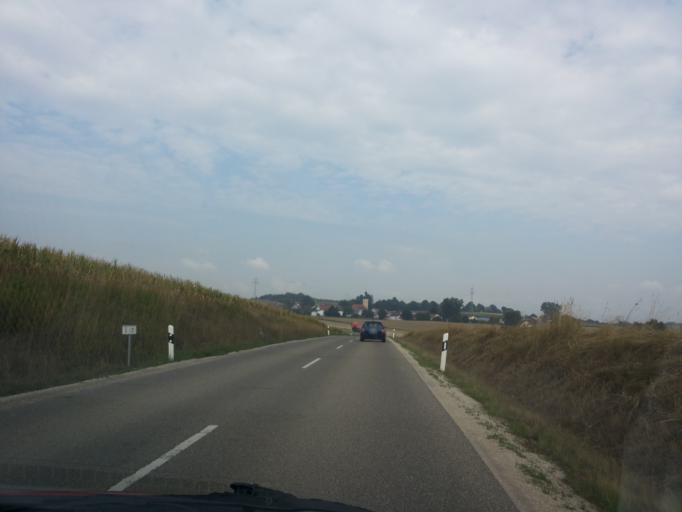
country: DE
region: Bavaria
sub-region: Upper Bavaria
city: Vohburg an der Donau
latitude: 48.7913
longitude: 11.5851
